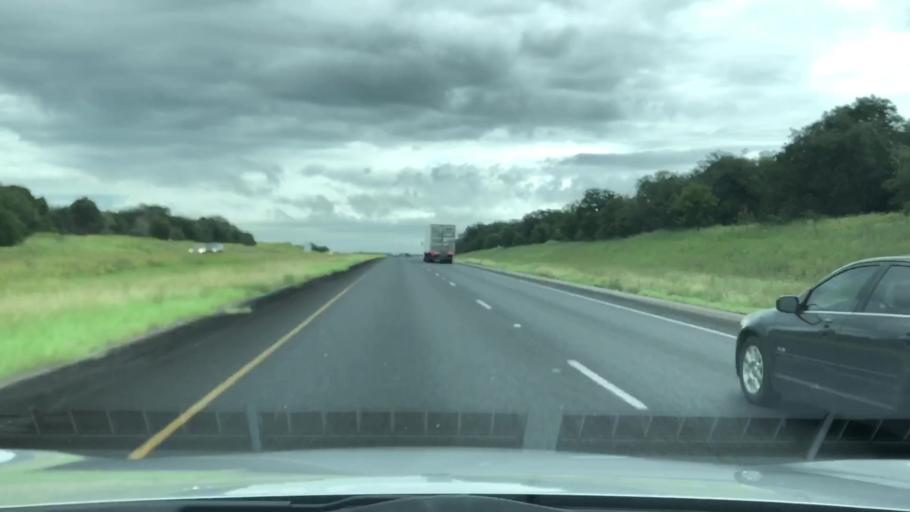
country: US
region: Texas
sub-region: Gonzales County
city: Waelder
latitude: 29.6604
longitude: -97.3984
